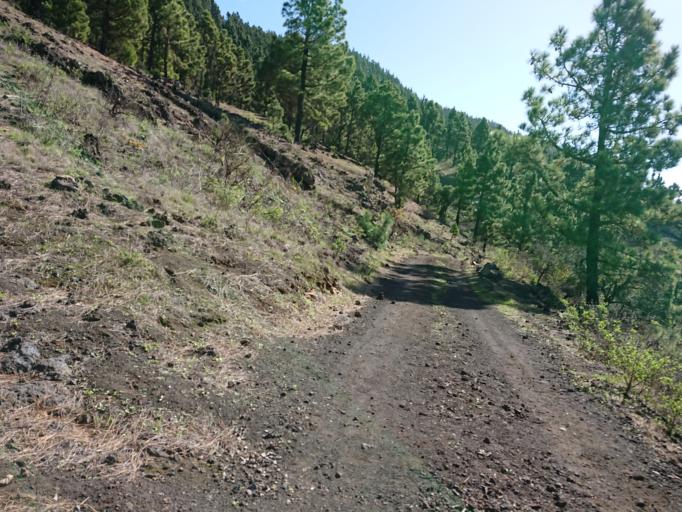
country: ES
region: Canary Islands
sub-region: Provincia de Santa Cruz de Tenerife
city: El Paso
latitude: 28.6070
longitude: -17.8667
